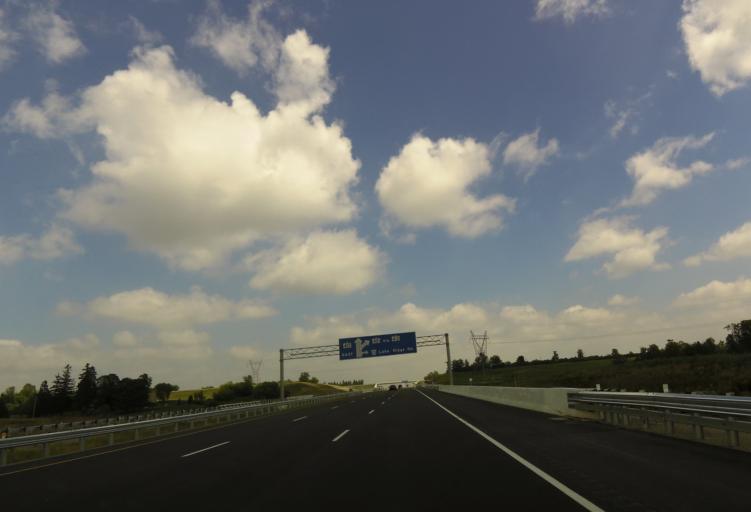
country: CA
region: Ontario
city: Ajax
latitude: 43.9444
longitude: -79.0429
